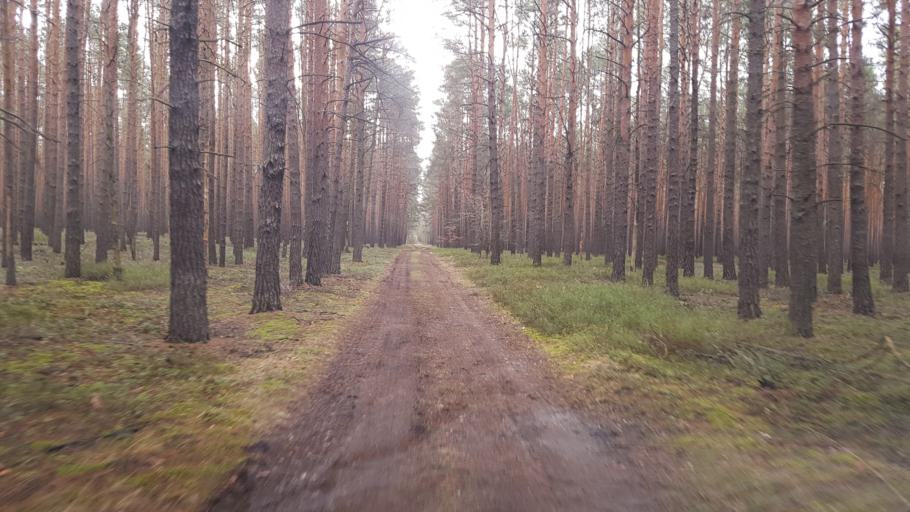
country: DE
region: Brandenburg
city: Sallgast
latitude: 51.6066
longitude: 13.8212
